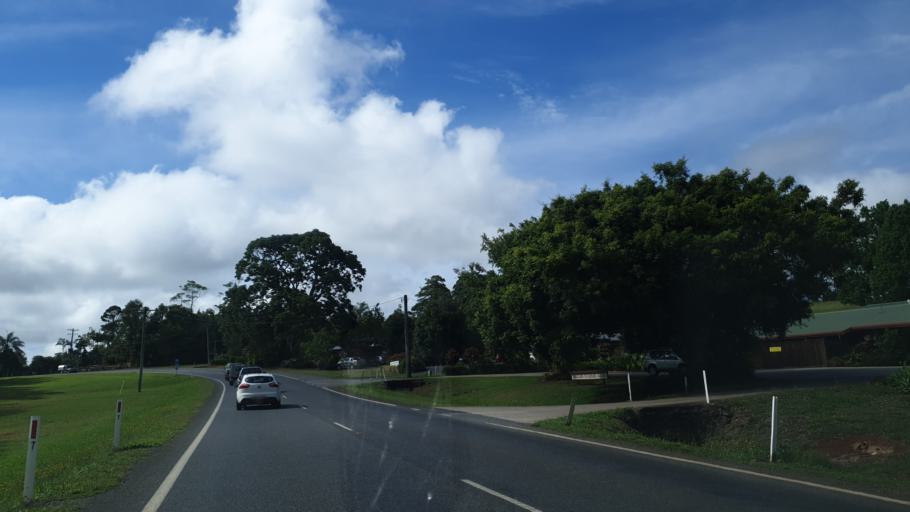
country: AU
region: Queensland
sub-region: Tablelands
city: Atherton
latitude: -17.3537
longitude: 145.5834
